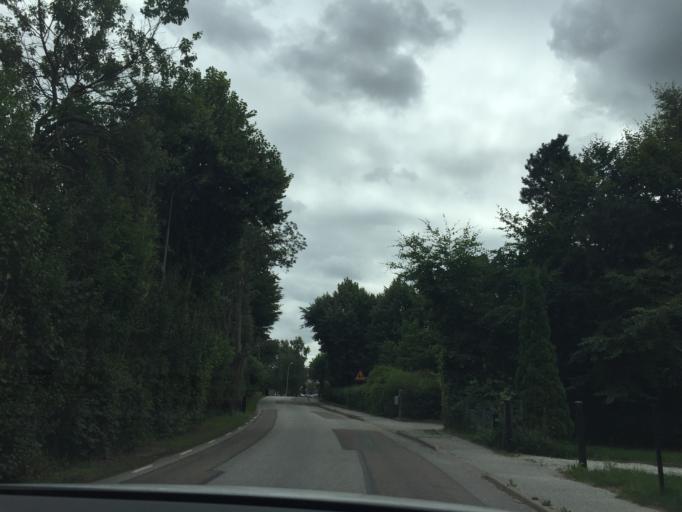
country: SE
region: Skane
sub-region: Sjobo Kommun
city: Blentarp
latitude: 55.5860
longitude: 13.6007
